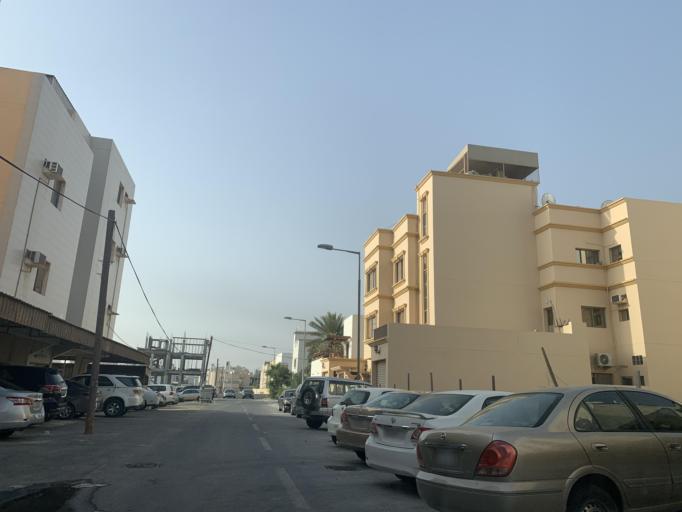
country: BH
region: Northern
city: Madinat `Isa
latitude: 26.1914
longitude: 50.5635
